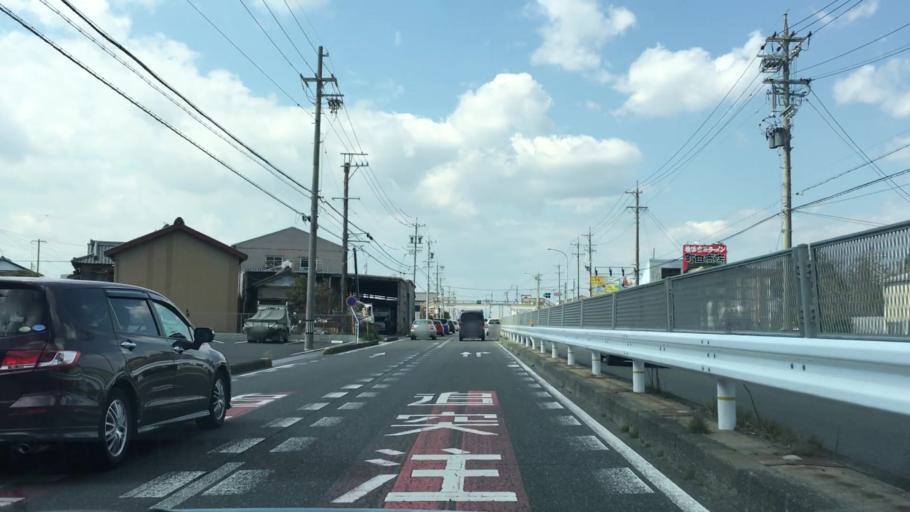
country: JP
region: Aichi
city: Toyohashi
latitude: 34.7390
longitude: 137.4223
